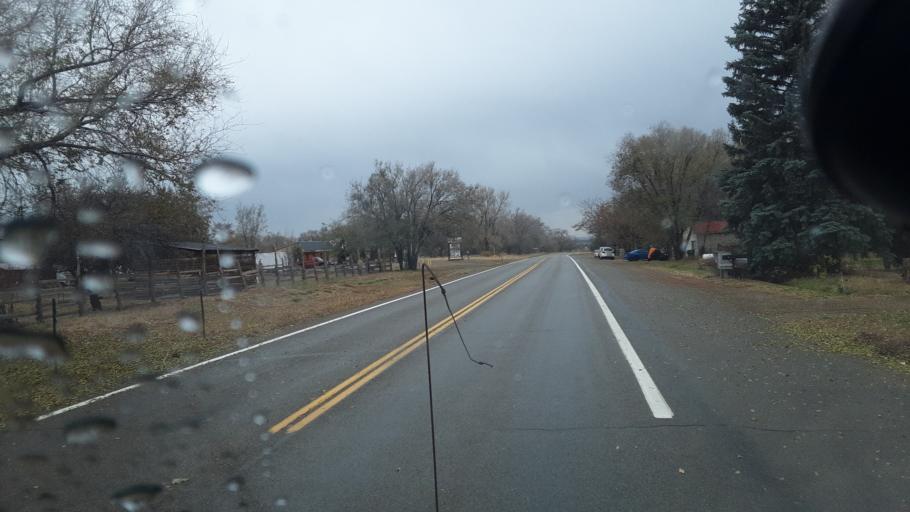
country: US
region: Colorado
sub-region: Montezuma County
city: Mancos
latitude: 37.0944
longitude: -108.1701
